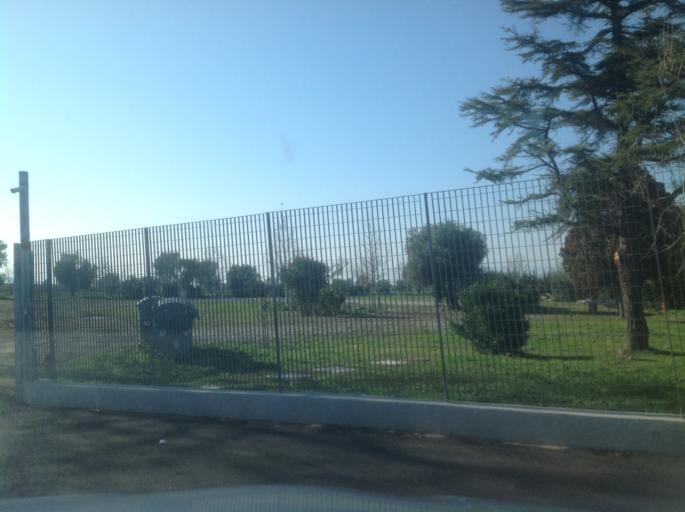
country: IT
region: Calabria
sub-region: Provincia di Cosenza
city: Sibari
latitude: 39.7183
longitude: 16.4909
